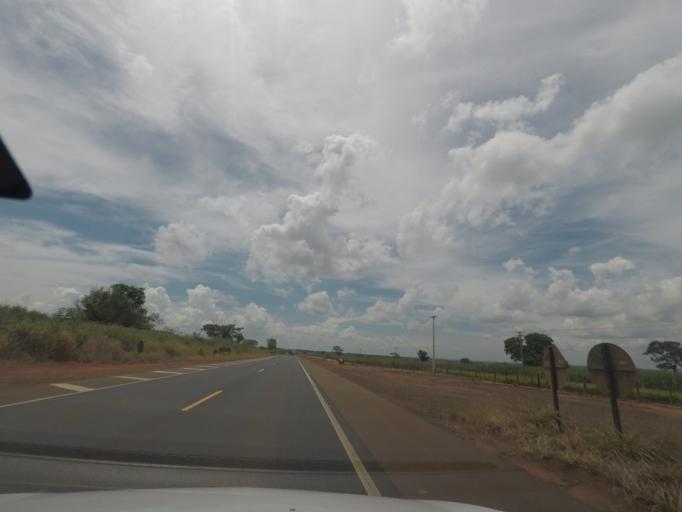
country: BR
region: Sao Paulo
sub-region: Barretos
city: Barretos
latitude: -20.3862
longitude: -48.6410
